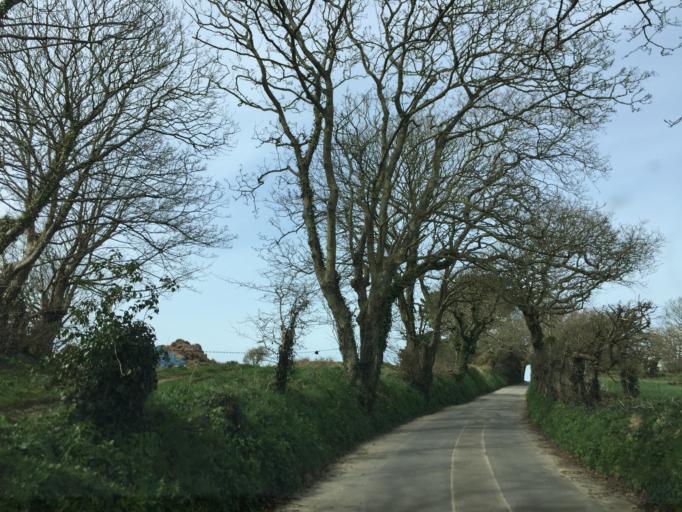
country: JE
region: St Helier
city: Saint Helier
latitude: 49.2430
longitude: -2.1741
